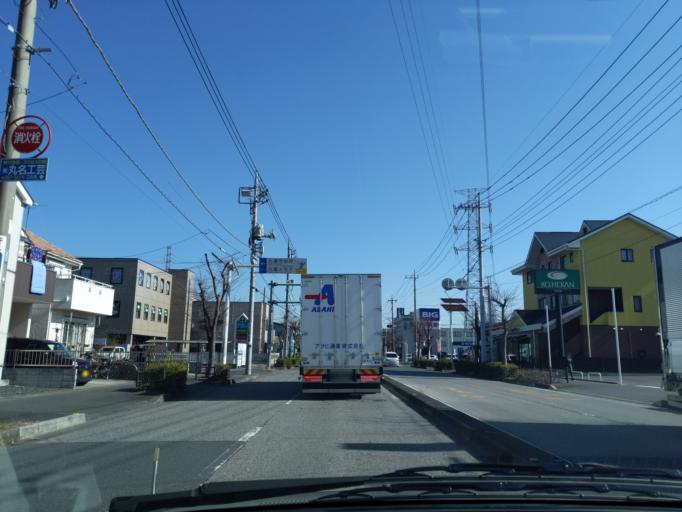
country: JP
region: Saitama
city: Yashio-shi
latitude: 35.8206
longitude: 139.8376
